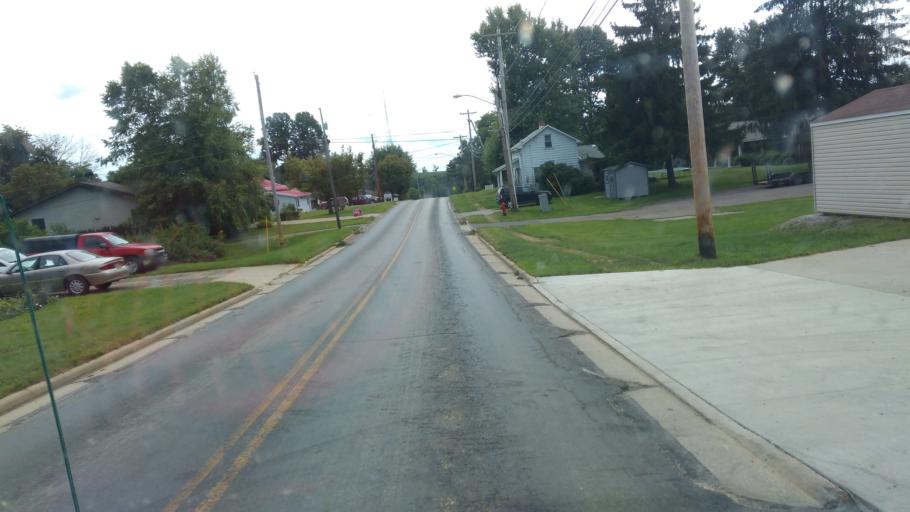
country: US
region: Ohio
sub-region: Holmes County
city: Millersburg
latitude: 40.5602
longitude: -81.7974
